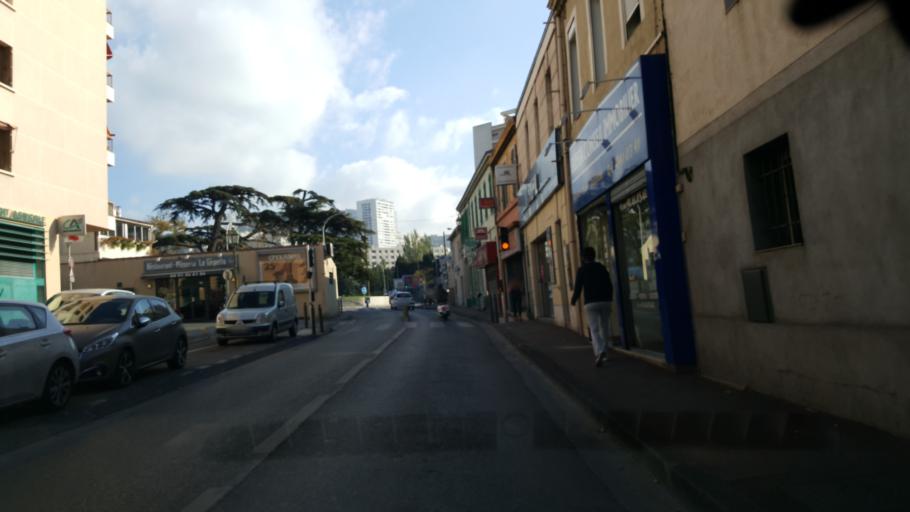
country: FR
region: Provence-Alpes-Cote d'Azur
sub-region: Departement des Bouches-du-Rhone
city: Marseille 09
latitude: 43.2577
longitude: 5.4182
